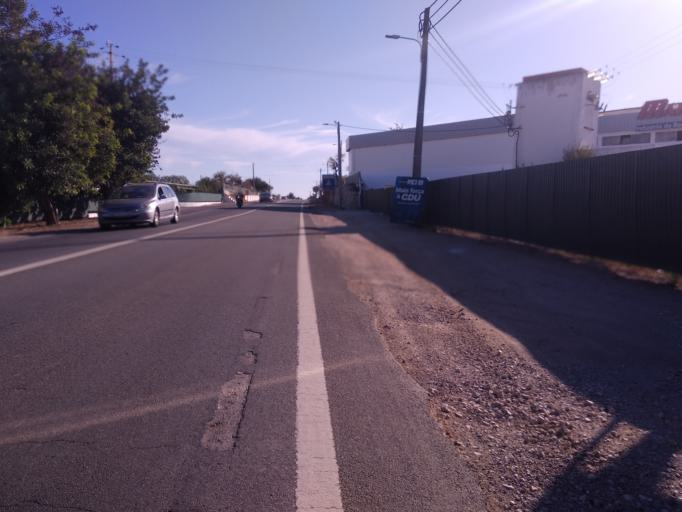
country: PT
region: Faro
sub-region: Sao Bras de Alportel
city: Sao Bras de Alportel
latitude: 37.0964
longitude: -7.9065
